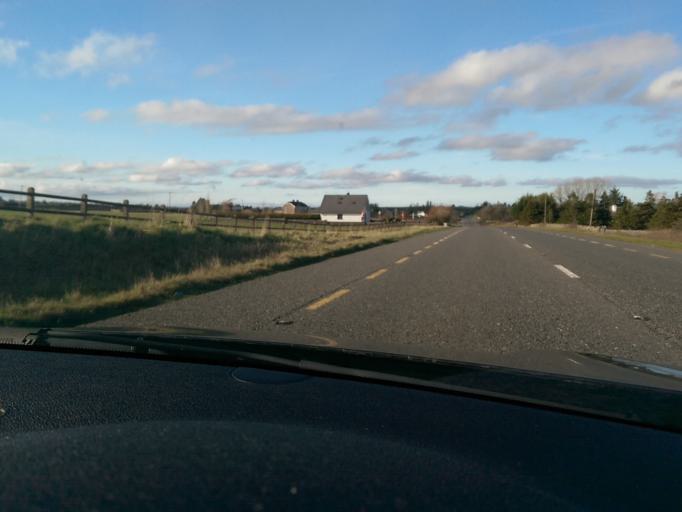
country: IE
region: Connaught
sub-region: Roscommon
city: Roscommon
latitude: 53.6707
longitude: -8.1977
